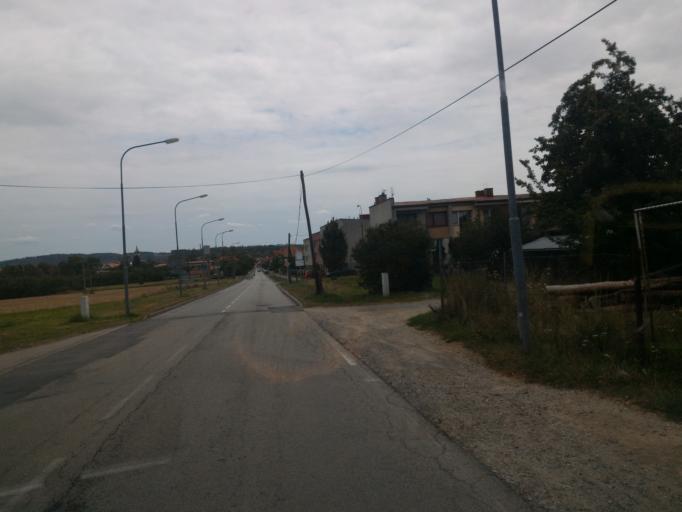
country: CZ
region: Vysocina
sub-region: Okres Jihlava
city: Telc
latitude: 49.1838
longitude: 15.4407
